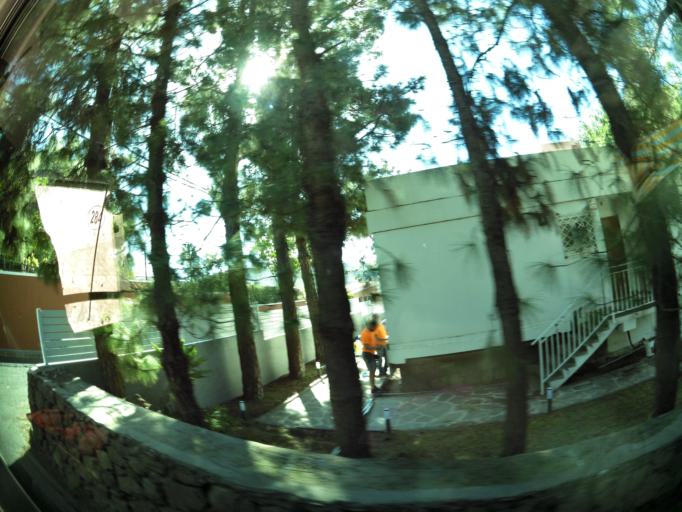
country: ES
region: Canary Islands
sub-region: Provincia de Las Palmas
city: Santa Brigida
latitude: 28.0442
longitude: -15.4761
